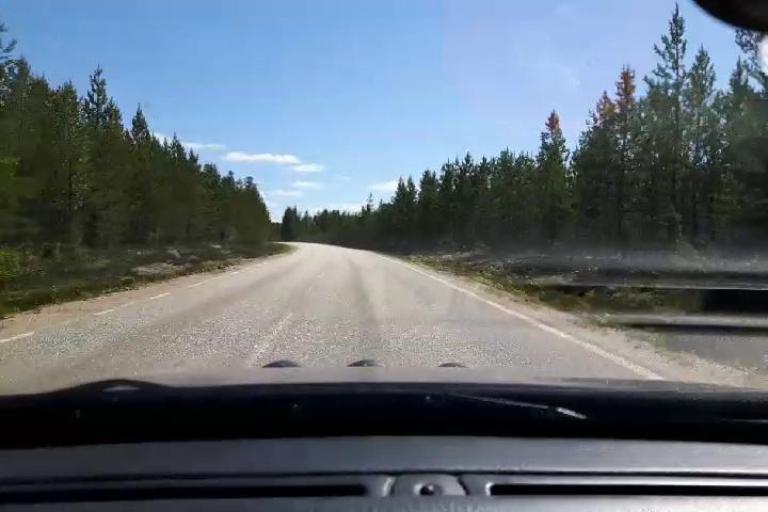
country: SE
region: Jaemtland
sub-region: Harjedalens Kommun
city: Sveg
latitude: 62.1174
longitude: 15.0431
